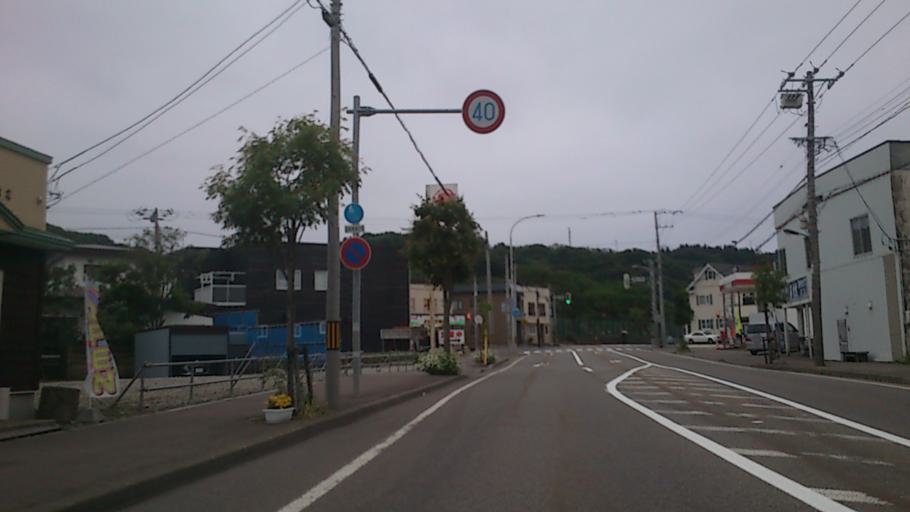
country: JP
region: Hokkaido
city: Kamiiso
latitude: 41.9707
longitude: 140.1382
